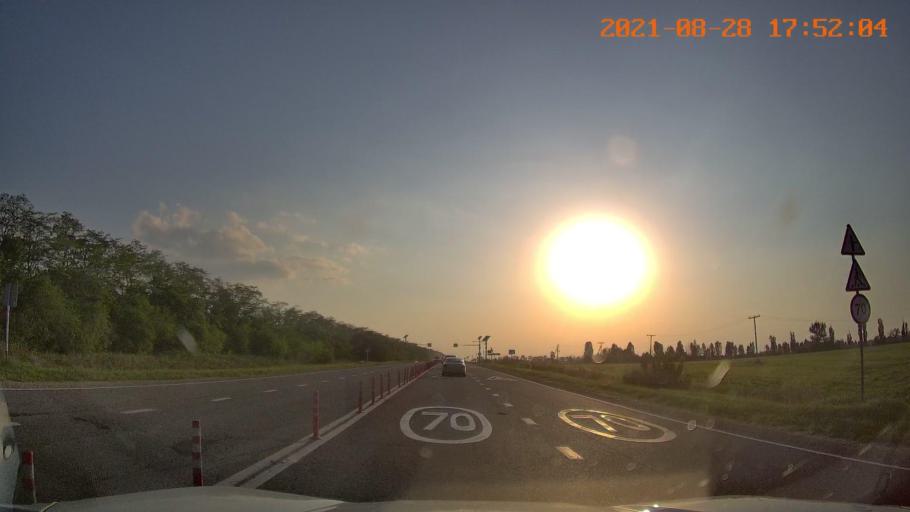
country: RU
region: Krasnodarskiy
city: Konstantinovskaya
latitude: 44.9416
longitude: 40.7803
